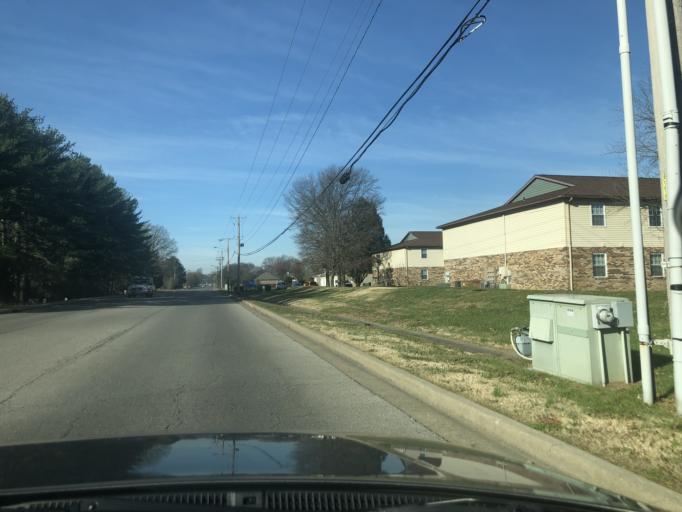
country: US
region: Indiana
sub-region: Warrick County
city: Newburgh
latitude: 37.9696
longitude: -87.4529
